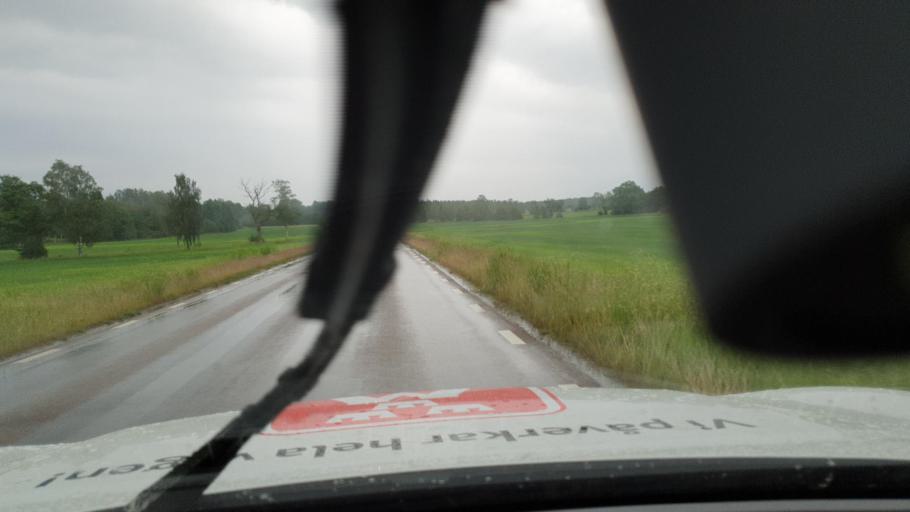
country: SE
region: Vaestra Goetaland
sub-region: Mariestads Kommun
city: Mariestad
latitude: 58.7595
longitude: 13.9108
